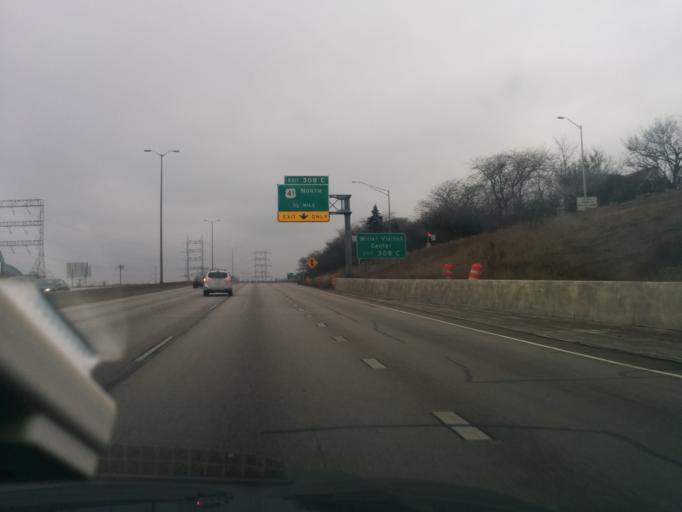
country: US
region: Wisconsin
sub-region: Milwaukee County
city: West Milwaukee
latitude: 43.0323
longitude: -87.9593
